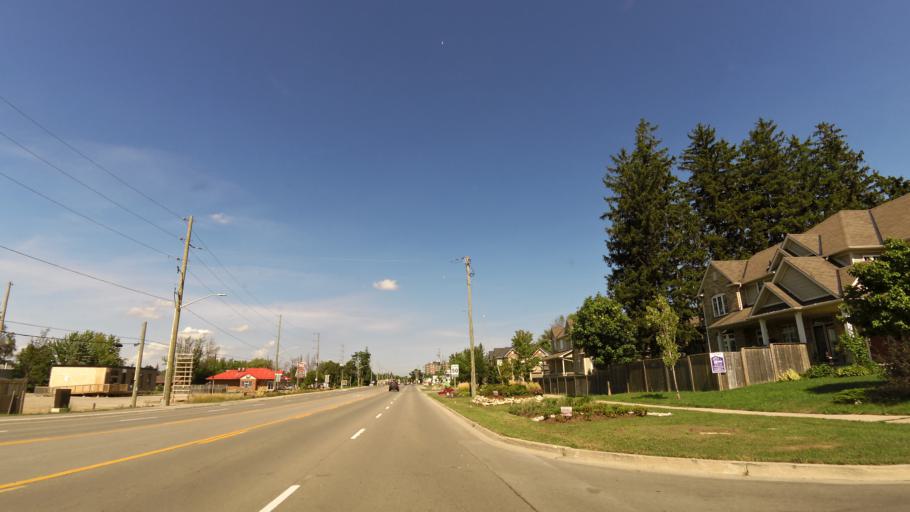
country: CA
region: Ontario
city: Burlington
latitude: 43.3267
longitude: -79.9005
